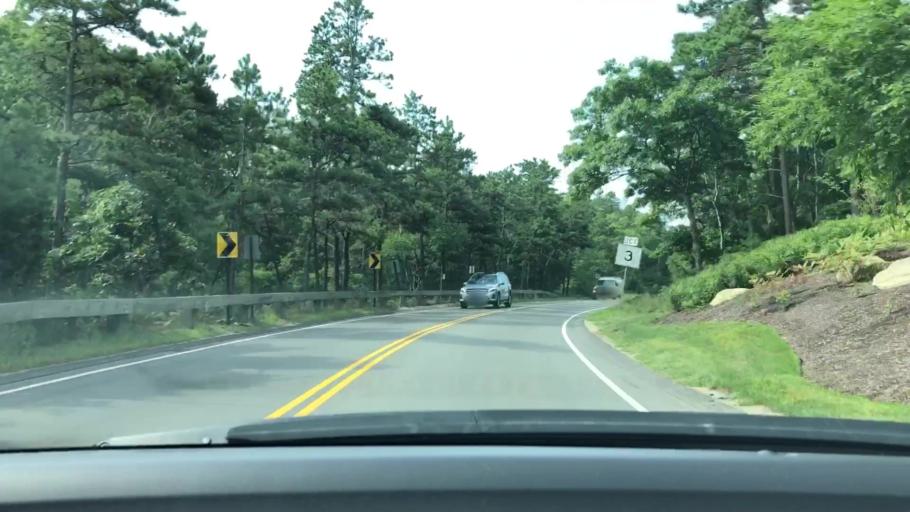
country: US
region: Massachusetts
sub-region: Plymouth County
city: White Island Shores
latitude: 41.8765
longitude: -70.5984
